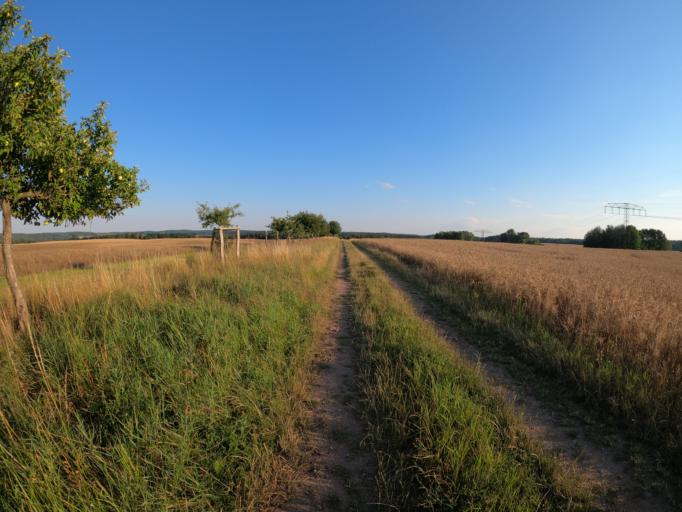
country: DE
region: Brandenburg
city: Althuttendorf
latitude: 53.0322
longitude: 13.8671
